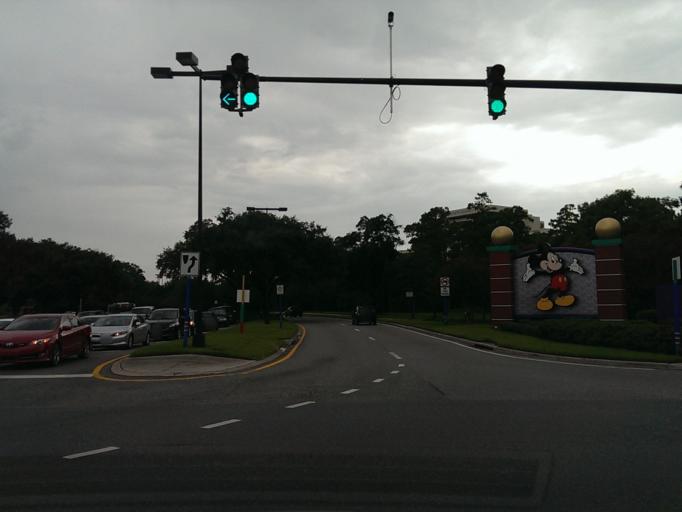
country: US
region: Florida
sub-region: Osceola County
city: Celebration
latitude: 28.3820
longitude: -81.5055
